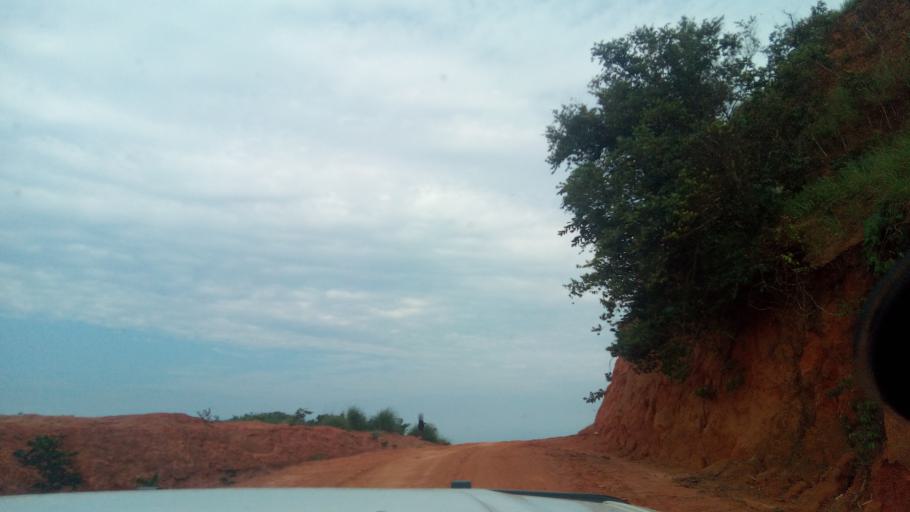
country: CD
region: Kasai-Oriental
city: Kabinda
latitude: -6.1650
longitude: 24.4437
